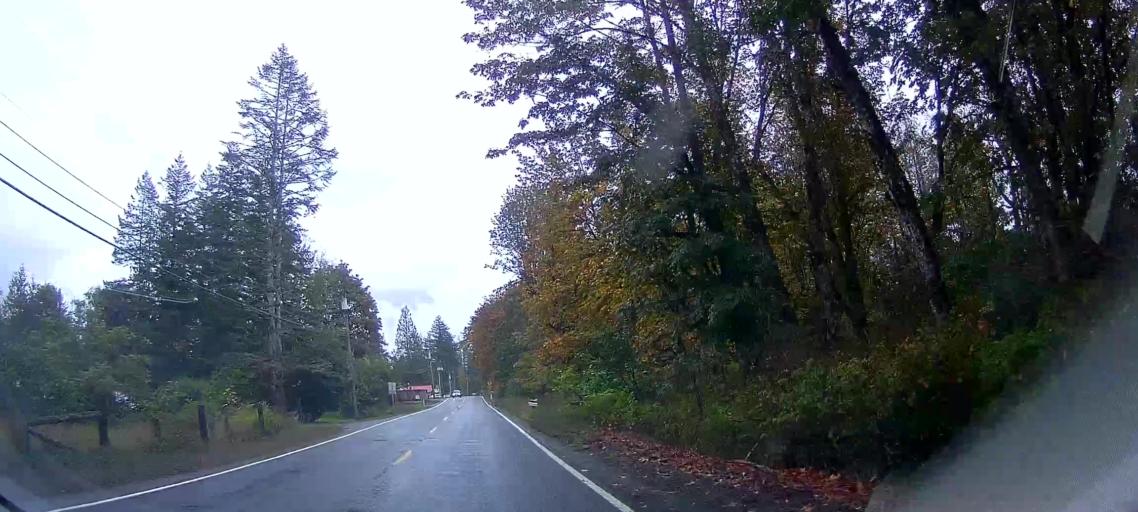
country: US
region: Washington
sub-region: Snohomish County
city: Darrington
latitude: 48.5252
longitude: -121.4563
